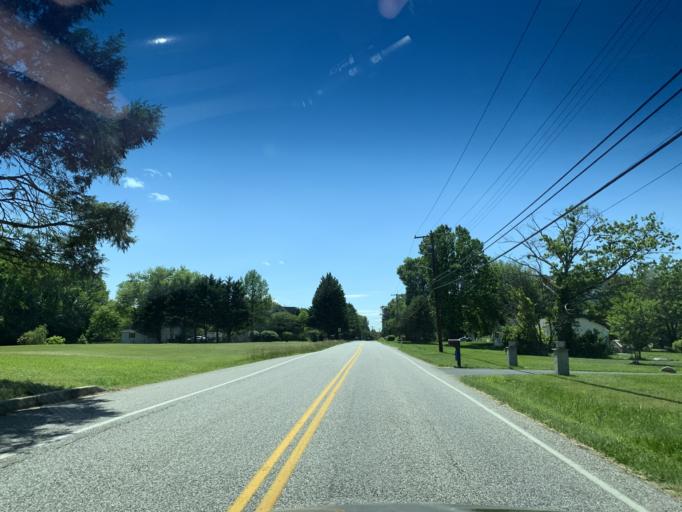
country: US
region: Maryland
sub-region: Harford County
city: Havre de Grace
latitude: 39.5544
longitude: -76.1393
